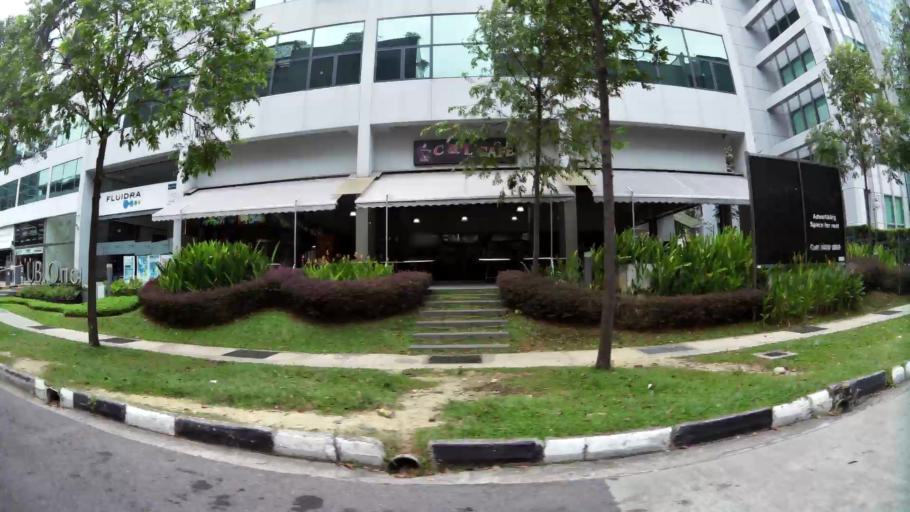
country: SG
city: Singapore
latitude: 1.3335
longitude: 103.8923
